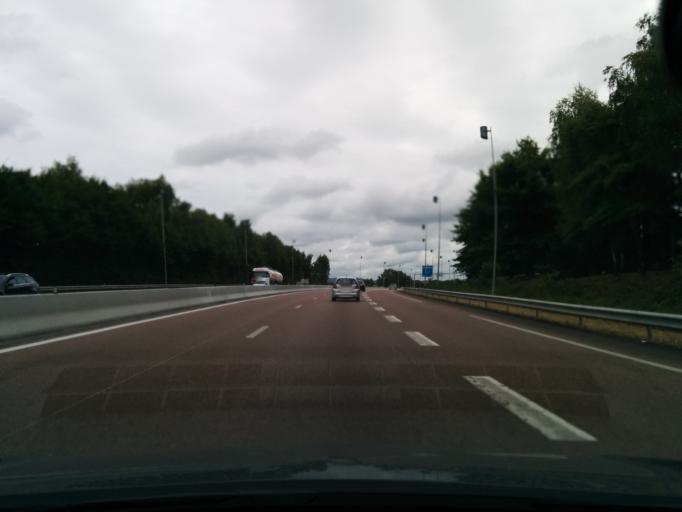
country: FR
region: Limousin
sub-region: Departement de la Haute-Vienne
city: Rilhac-Rancon
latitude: 45.8776
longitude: 1.2880
